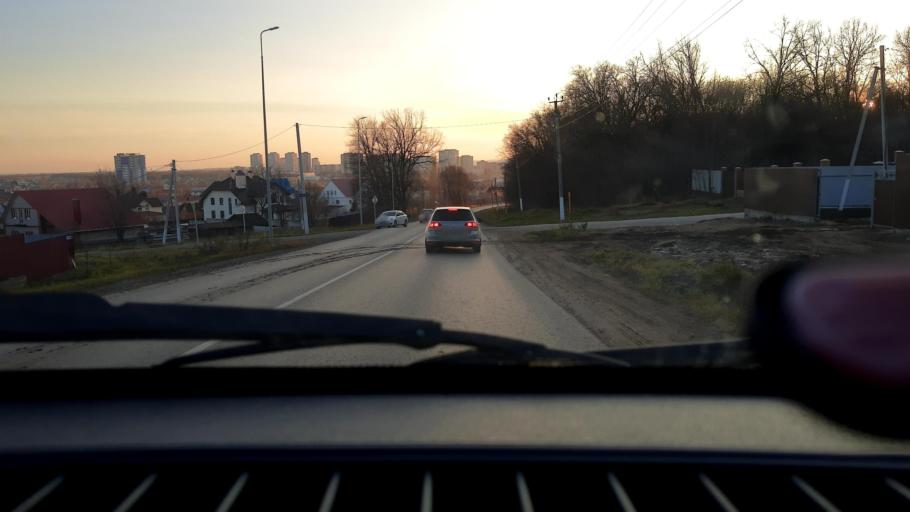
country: RU
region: Bashkortostan
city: Mikhaylovka
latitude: 54.8092
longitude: 55.8813
